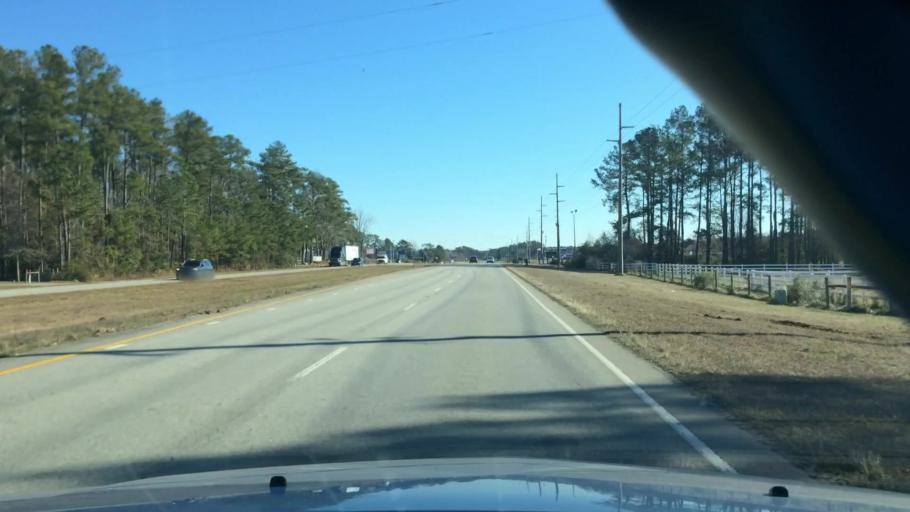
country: US
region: North Carolina
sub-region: Brunswick County
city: Shallotte
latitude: 33.9560
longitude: -78.4388
